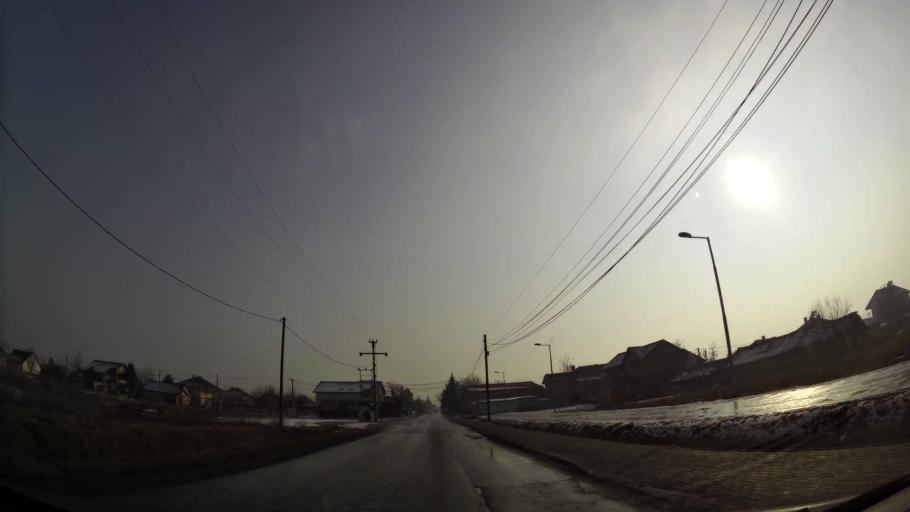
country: MK
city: Kadino
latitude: 41.9742
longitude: 21.5948
